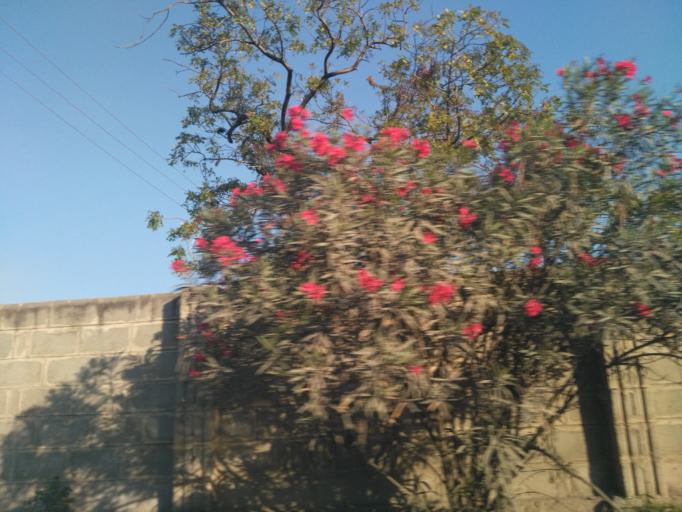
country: TZ
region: Dar es Salaam
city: Magomeni
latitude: -6.7667
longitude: 39.2592
